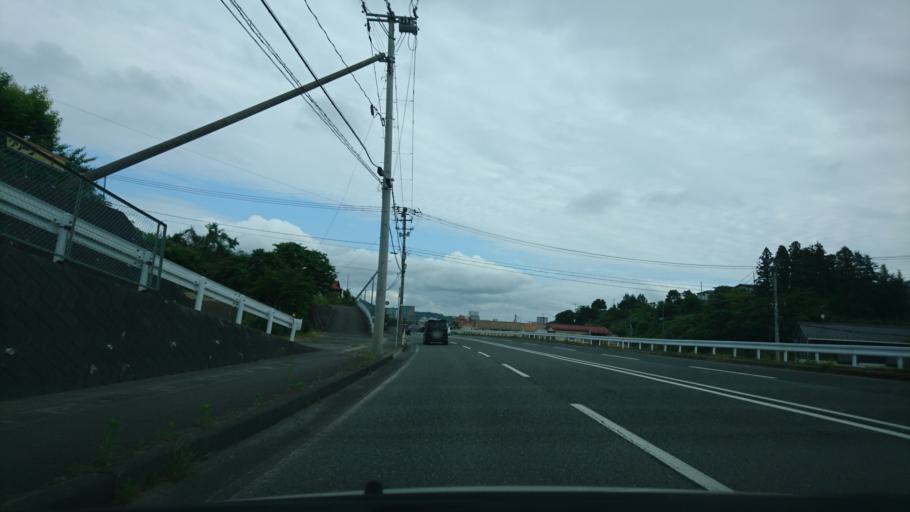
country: JP
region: Iwate
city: Ichinoseki
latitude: 38.9176
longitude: 141.1412
